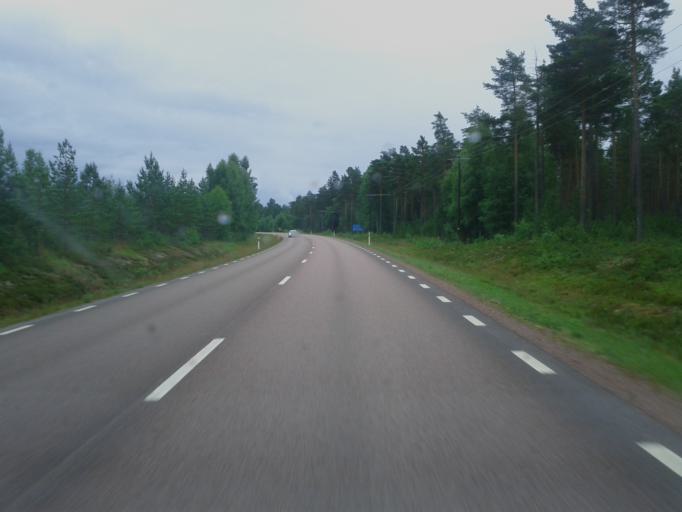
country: SE
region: Dalarna
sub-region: Mora Kommun
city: Mora
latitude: 61.0344
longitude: 14.5129
